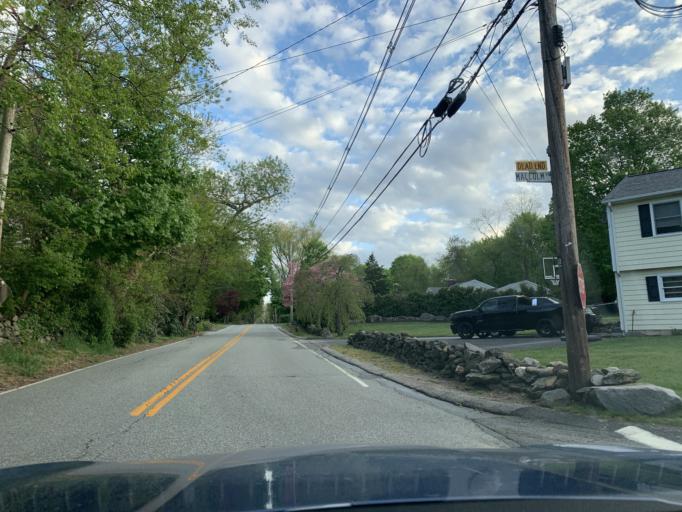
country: US
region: Rhode Island
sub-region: Kent County
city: East Greenwich
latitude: 41.6351
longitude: -71.4583
